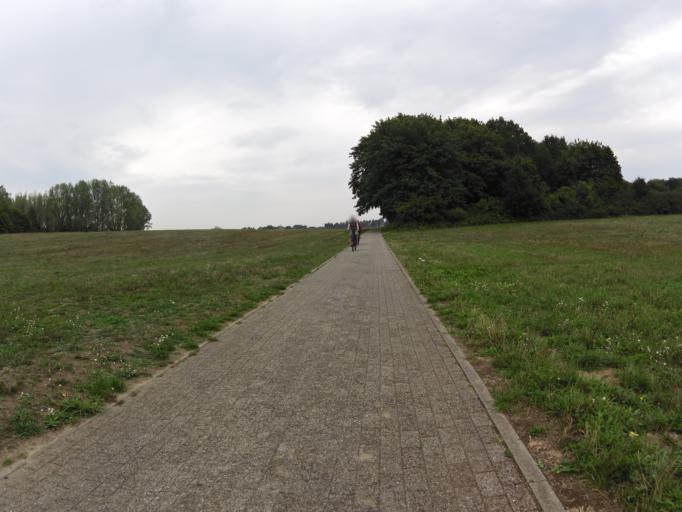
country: PL
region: West Pomeranian Voivodeship
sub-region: Swinoujscie
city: Swinoujscie
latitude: 53.8748
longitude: 14.1921
